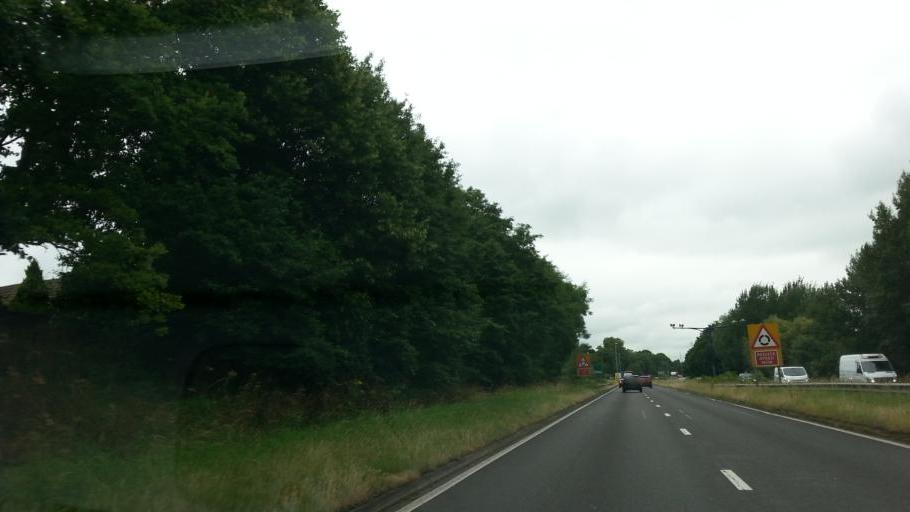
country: GB
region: England
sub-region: Northamptonshire
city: Northampton
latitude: 52.2622
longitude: -0.8416
